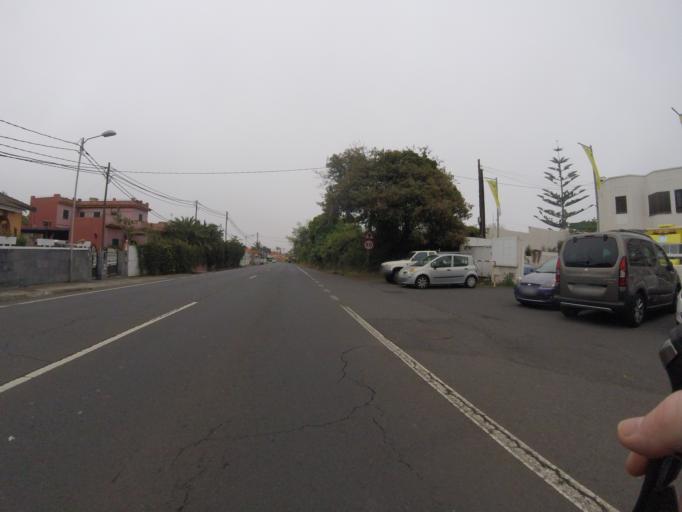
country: ES
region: Canary Islands
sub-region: Provincia de Santa Cruz de Tenerife
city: La Laguna
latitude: 28.4918
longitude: -16.3648
